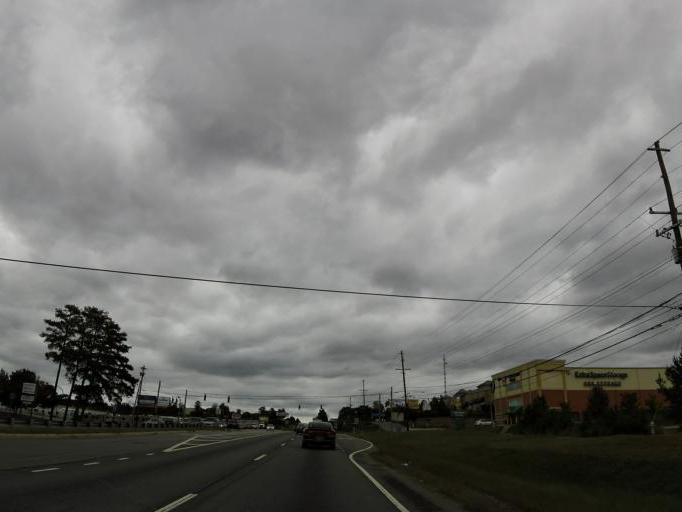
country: US
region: Georgia
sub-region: Cobb County
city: Marietta
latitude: 33.9866
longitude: -84.5707
